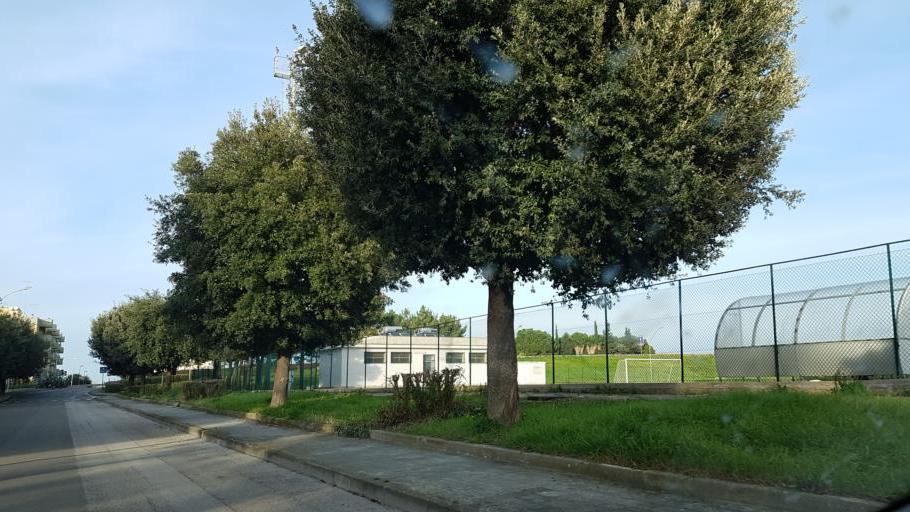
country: IT
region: Apulia
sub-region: Provincia di Brindisi
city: Brindisi
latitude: 40.6254
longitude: 17.9428
